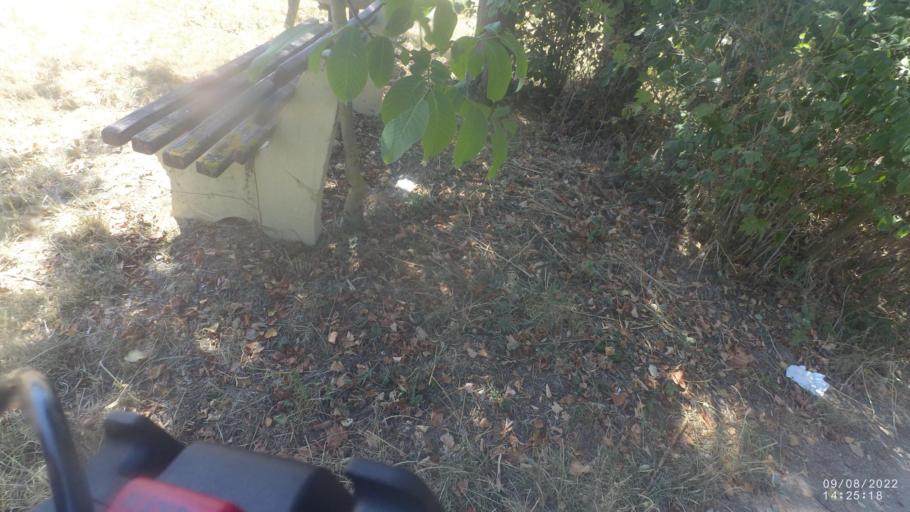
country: DE
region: Rheinland-Pfalz
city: Spiesheim
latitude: 49.8147
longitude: 8.1277
